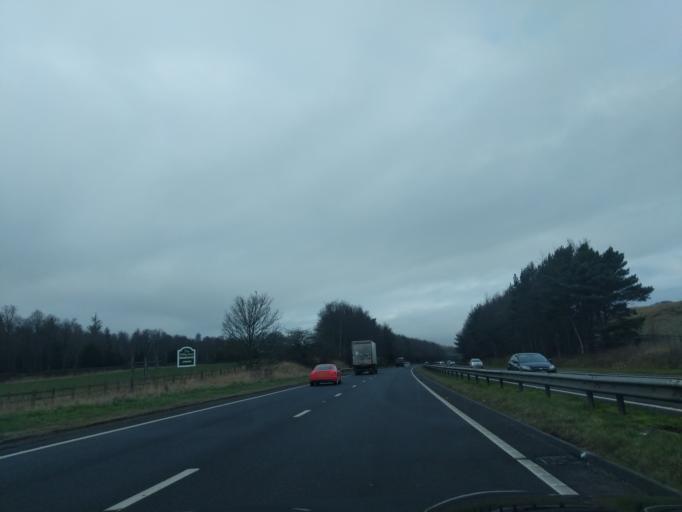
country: GB
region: England
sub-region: Northumberland
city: Stannington
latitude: 55.0890
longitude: -1.6541
